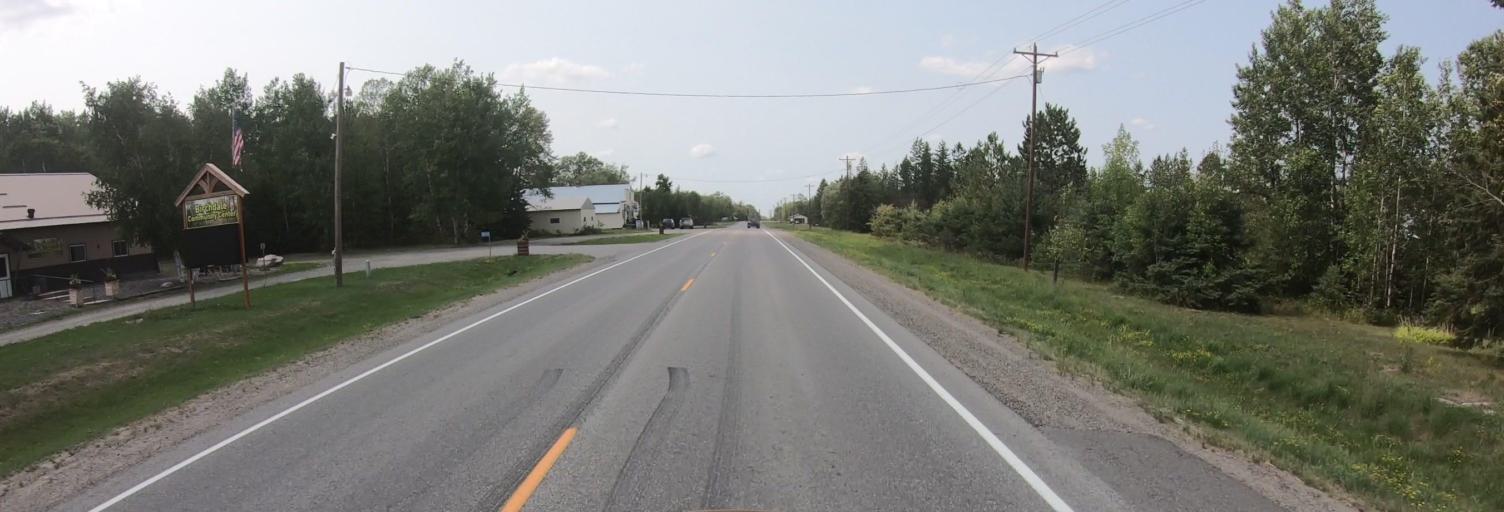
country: US
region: Minnesota
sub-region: Lake of the Woods County
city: Baudette
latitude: 48.6270
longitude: -94.0977
